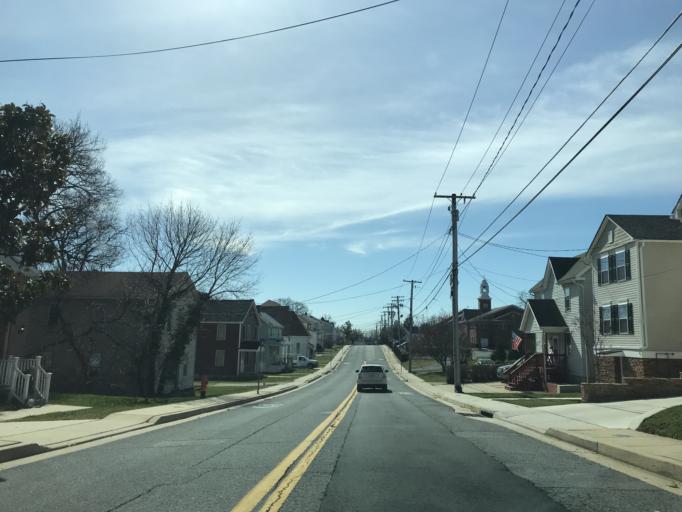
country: US
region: Maryland
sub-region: Baltimore County
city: Catonsville
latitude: 39.2751
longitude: -76.7384
